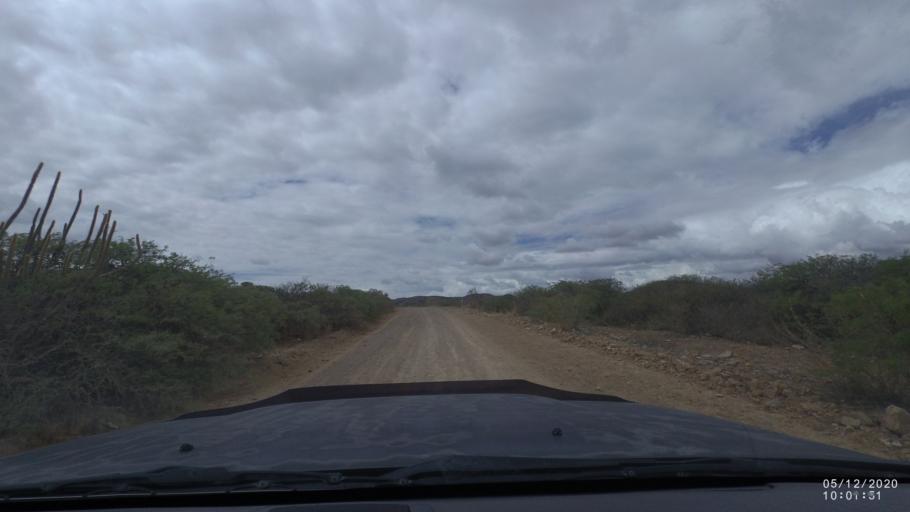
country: BO
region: Cochabamba
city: Sipe Sipe
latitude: -17.4451
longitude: -66.2872
